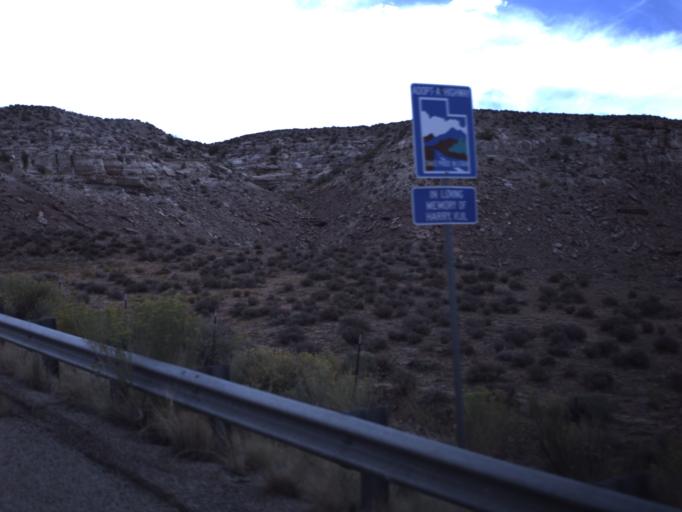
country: US
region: Utah
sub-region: San Juan County
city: Blanding
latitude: 37.2819
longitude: -109.3806
